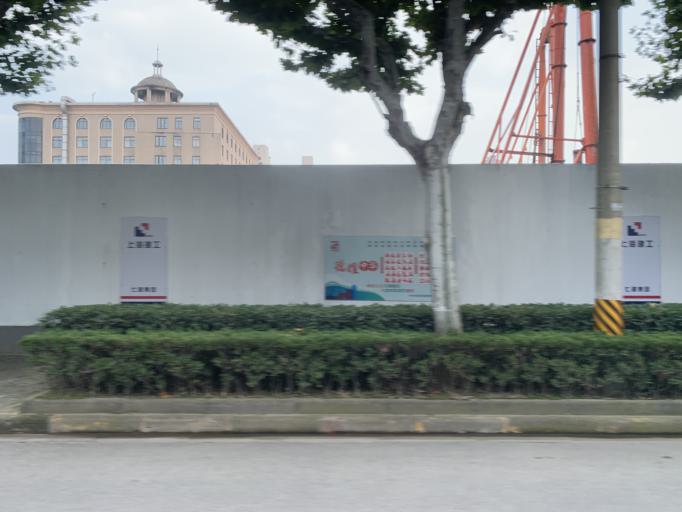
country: CN
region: Shanghai Shi
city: Pudong
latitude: 31.2381
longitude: 121.5269
